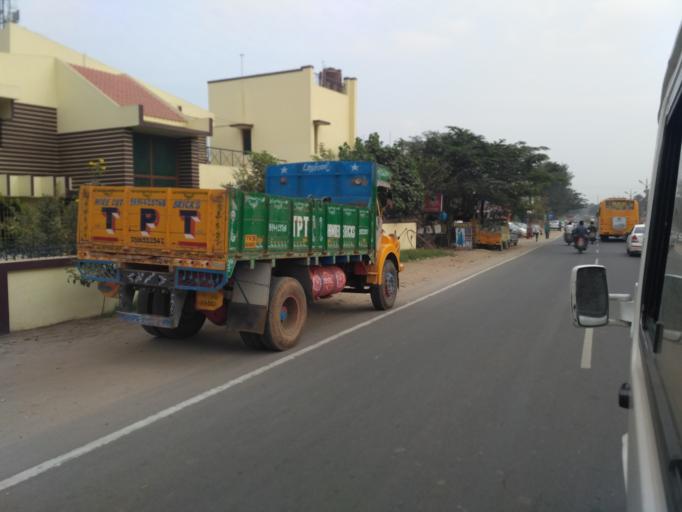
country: IN
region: Tamil Nadu
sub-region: Coimbatore
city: Periyanayakkanpalaiyam
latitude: 11.1119
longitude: 76.9361
